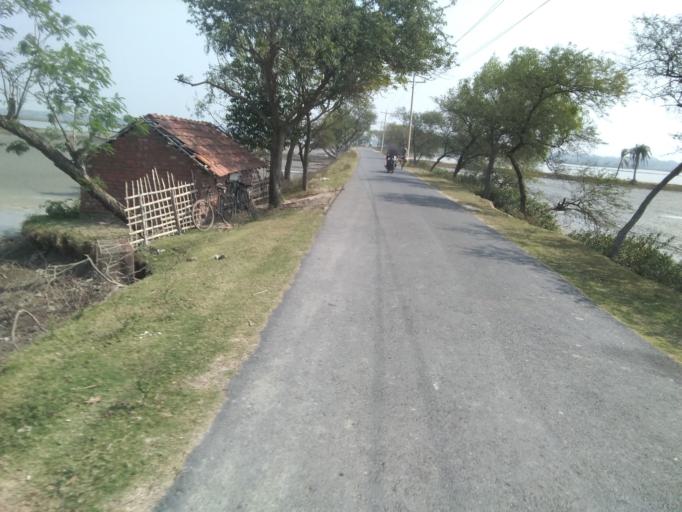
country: IN
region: West Bengal
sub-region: North 24 Parganas
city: Taki
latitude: 22.5939
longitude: 88.9813
